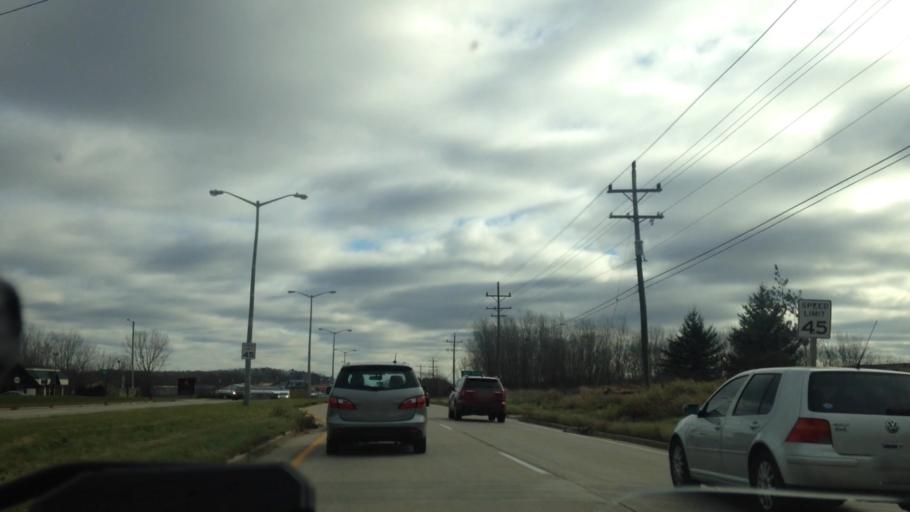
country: US
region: Wisconsin
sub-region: Washington County
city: West Bend
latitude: 43.4273
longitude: -88.2366
